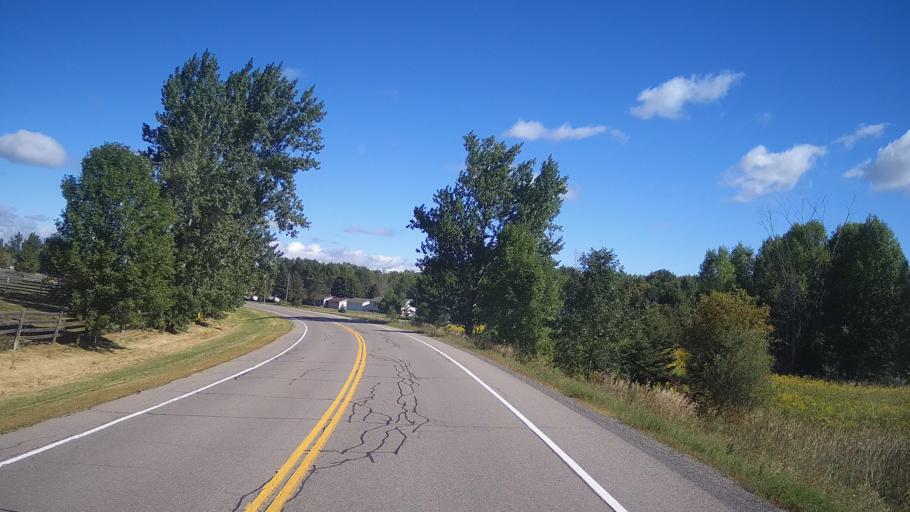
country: US
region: New York
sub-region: St. Lawrence County
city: Norfolk
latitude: 44.9524
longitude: -75.2802
